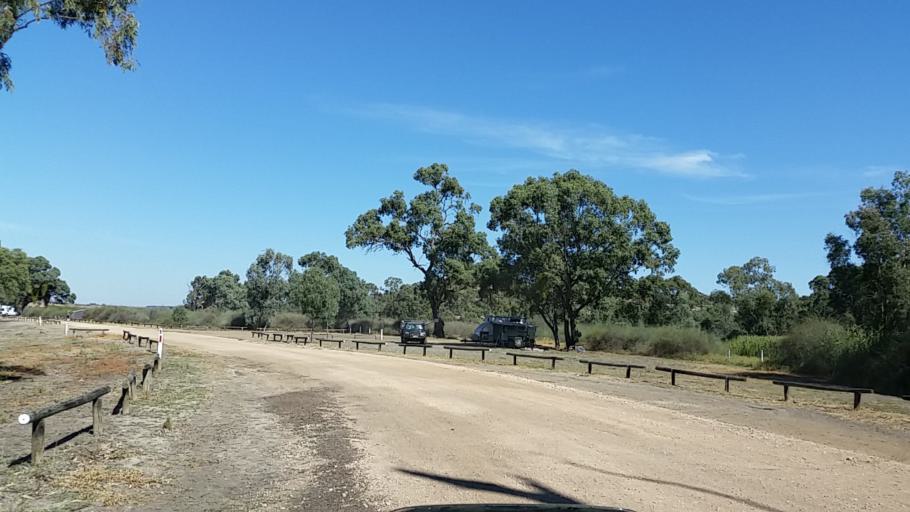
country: AU
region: South Australia
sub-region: Mid Murray
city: Mannum
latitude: -34.6998
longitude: 139.5765
